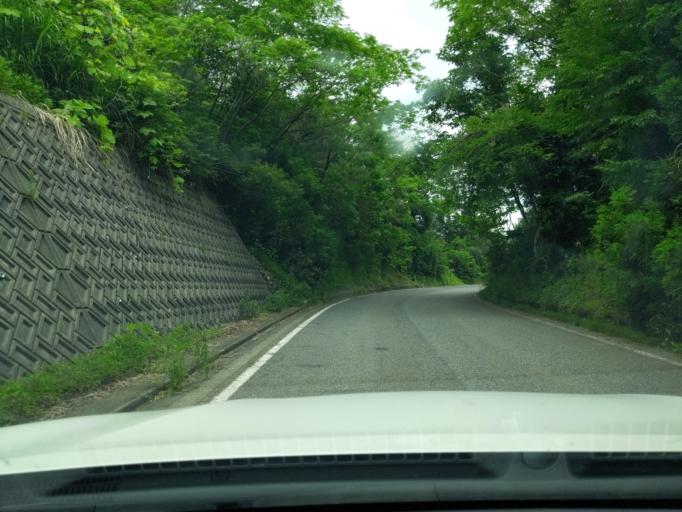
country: JP
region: Niigata
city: Kashiwazaki
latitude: 37.3408
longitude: 138.5897
